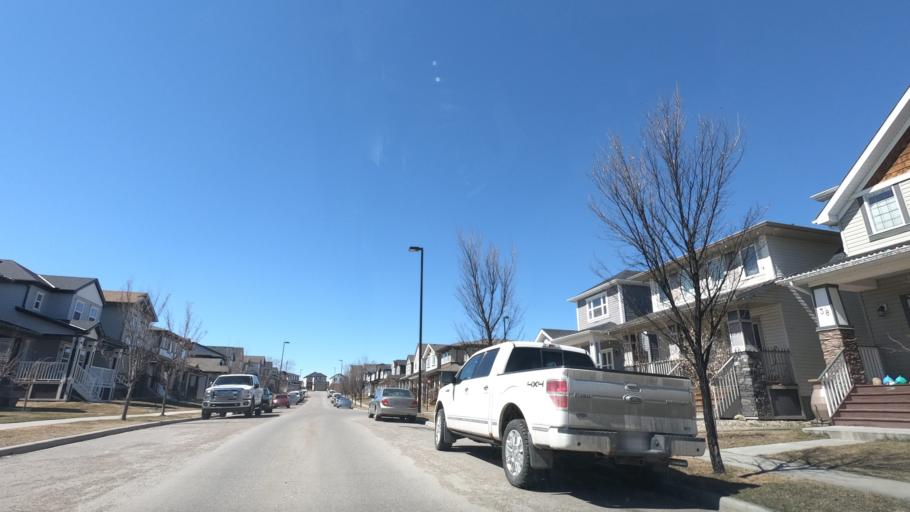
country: CA
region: Alberta
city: Airdrie
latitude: 51.3057
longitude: -114.0445
